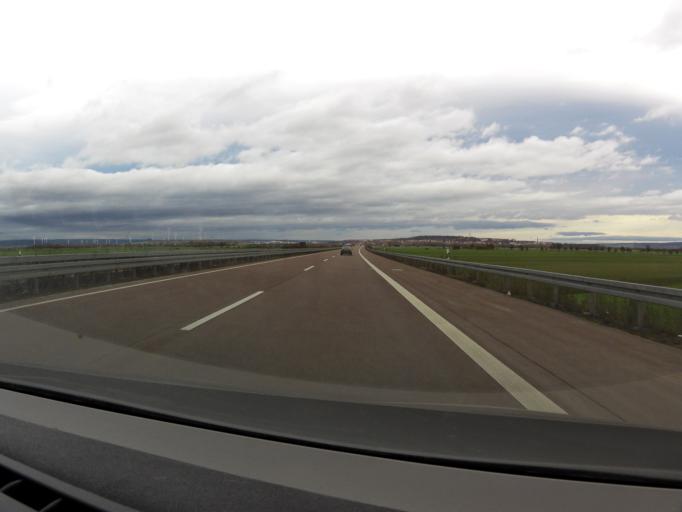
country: DE
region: Thuringia
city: Reinsdorf
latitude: 51.3449
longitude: 11.2614
